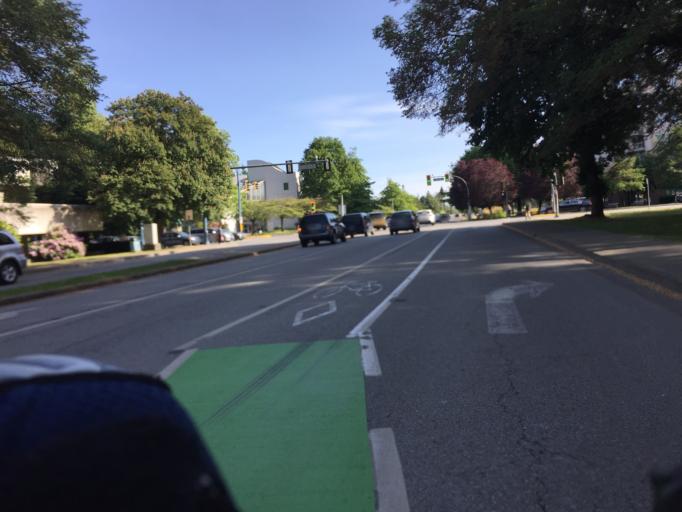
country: CA
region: British Columbia
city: Richmond
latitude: 49.1634
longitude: -123.1404
